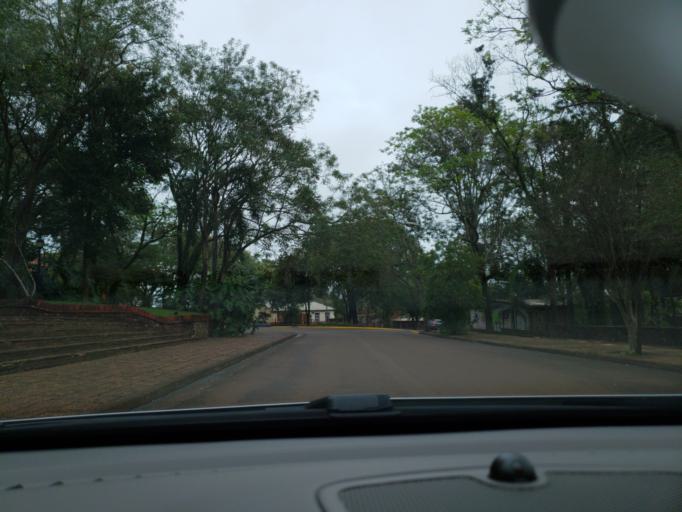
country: AR
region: Misiones
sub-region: Departamento de Apostoles
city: Apostoles
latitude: -27.9135
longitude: -55.7547
